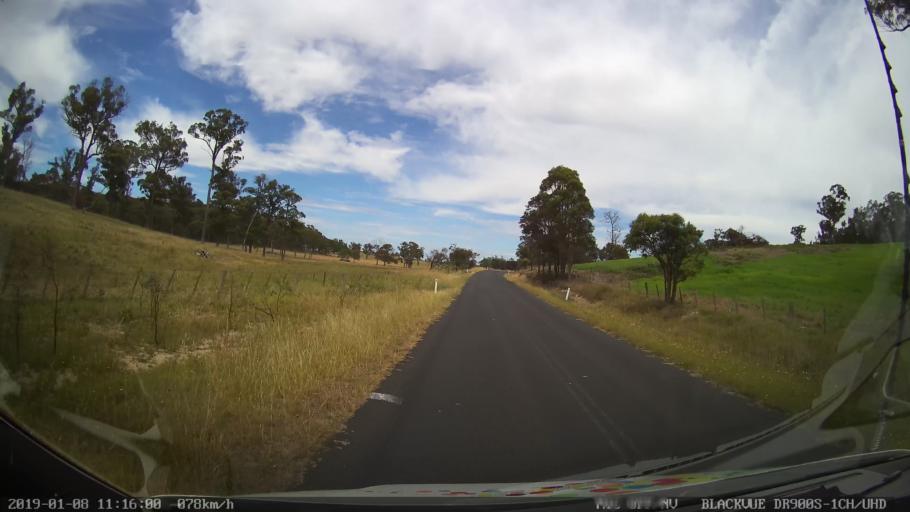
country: AU
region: New South Wales
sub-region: Guyra
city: Guyra
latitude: -30.2219
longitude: 151.5697
